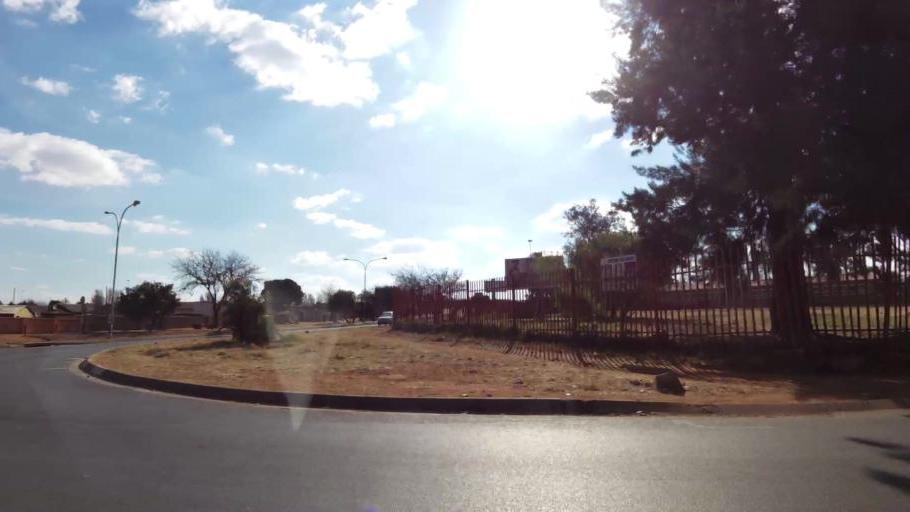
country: ZA
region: Gauteng
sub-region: City of Johannesburg Metropolitan Municipality
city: Soweto
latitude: -26.2357
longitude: 27.8781
